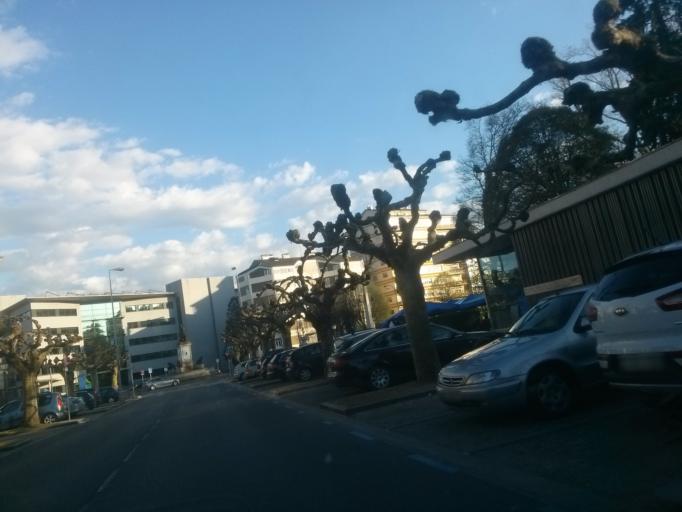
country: ES
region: Galicia
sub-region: Provincia de Lugo
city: Lugo
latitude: 43.0065
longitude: -7.5586
